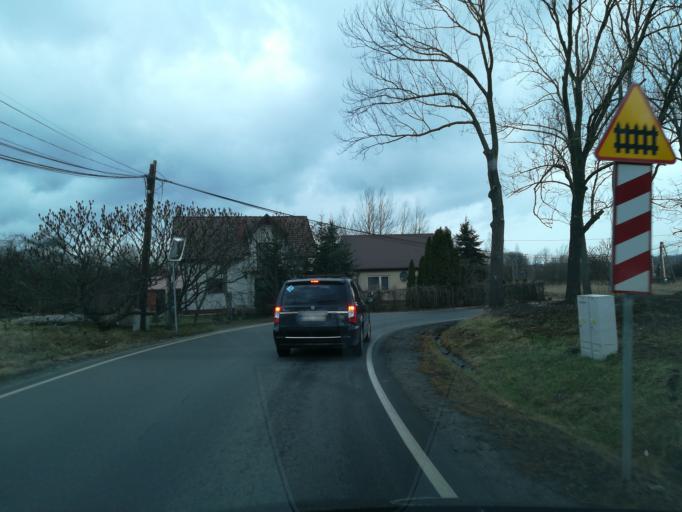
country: PL
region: Lesser Poland Voivodeship
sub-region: Krakow
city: Sidzina
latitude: 49.9842
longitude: 19.8727
